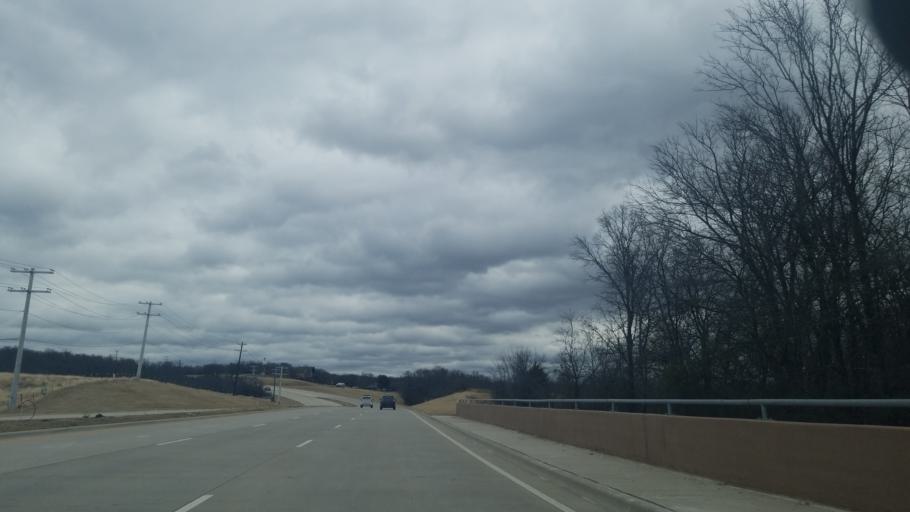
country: US
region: Texas
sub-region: Denton County
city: Trophy Club
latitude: 33.0494
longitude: -97.1791
